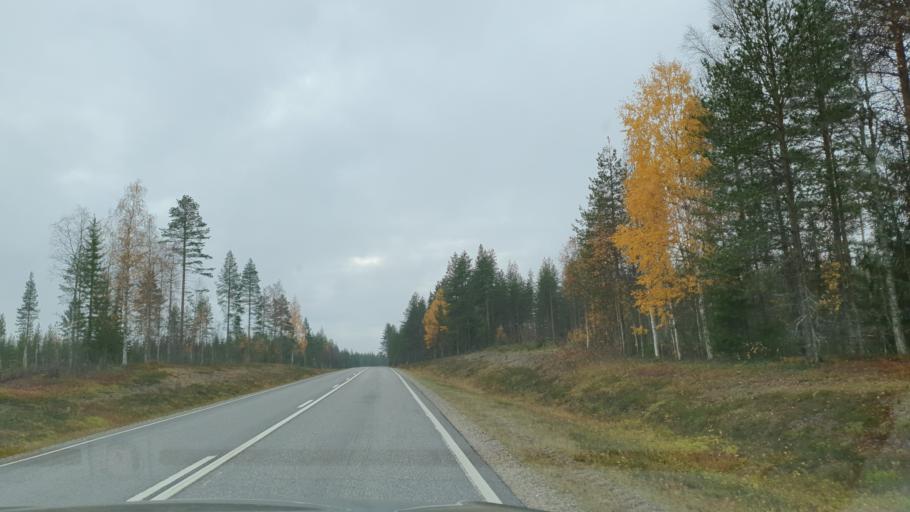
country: FI
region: Lapland
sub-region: Rovaniemi
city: Ranua
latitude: 66.0380
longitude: 26.3387
